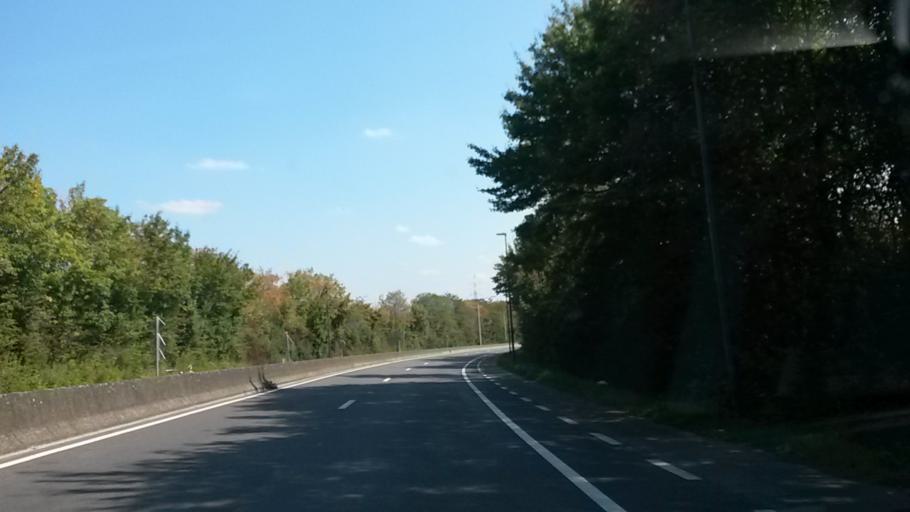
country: BE
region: Wallonia
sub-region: Province du Hainaut
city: Aiseau
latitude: 50.4464
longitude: 4.5856
